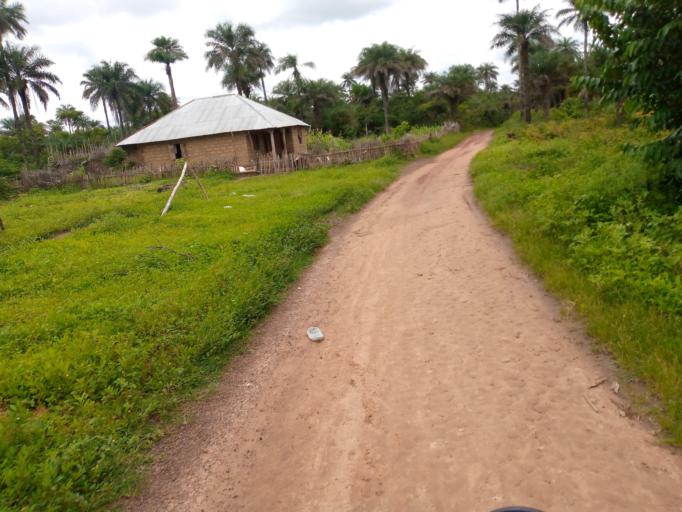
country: SL
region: Northern Province
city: Mange
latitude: 8.9905
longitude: -12.7944
